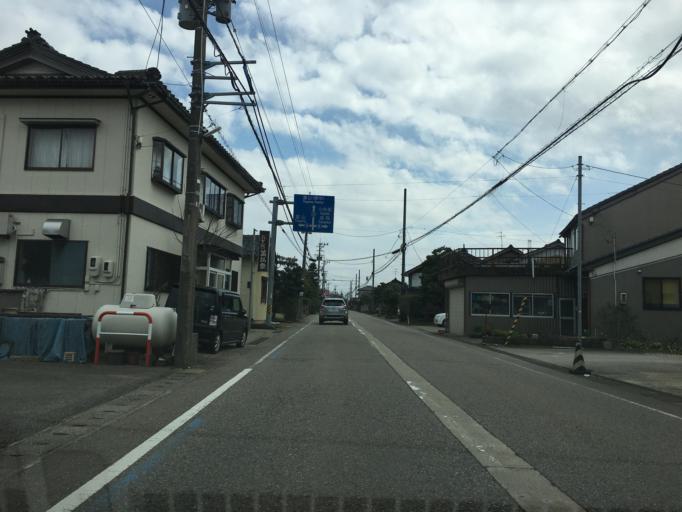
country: JP
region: Toyama
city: Kuragaki-kosugi
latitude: 36.6993
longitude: 137.1130
